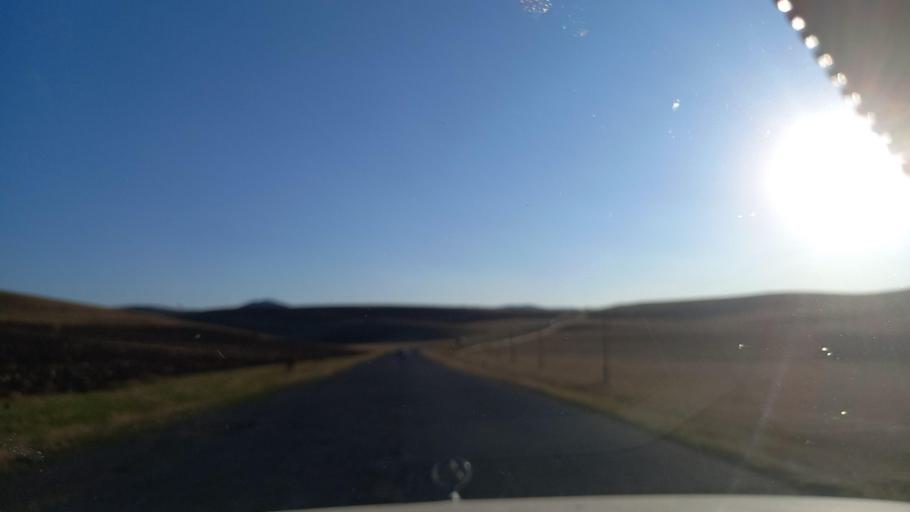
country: AZ
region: Shamkir Rayon
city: Shamkhor
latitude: 40.7627
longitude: 45.9201
